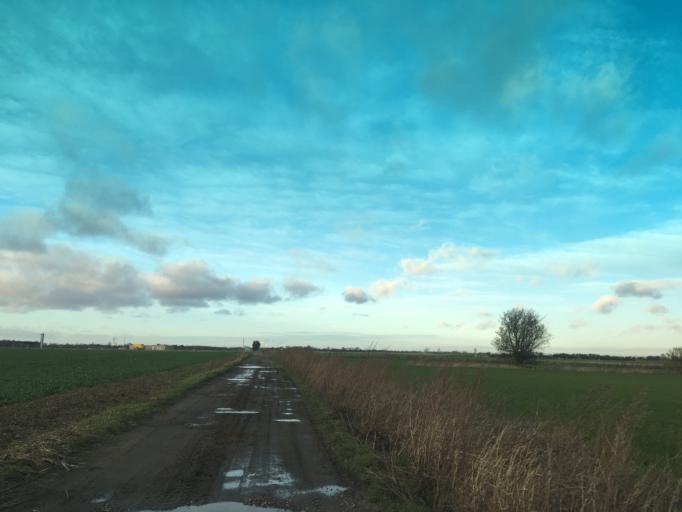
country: DK
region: Capital Region
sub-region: Tarnby Kommune
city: Tarnby
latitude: 55.5891
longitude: 12.6111
